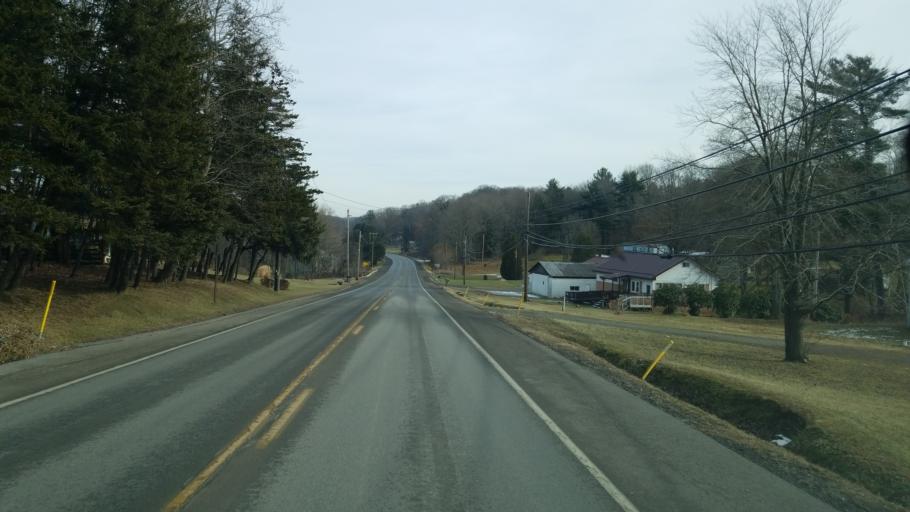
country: US
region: Pennsylvania
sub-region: Indiana County
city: Clymer
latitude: 40.7055
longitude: -78.9781
